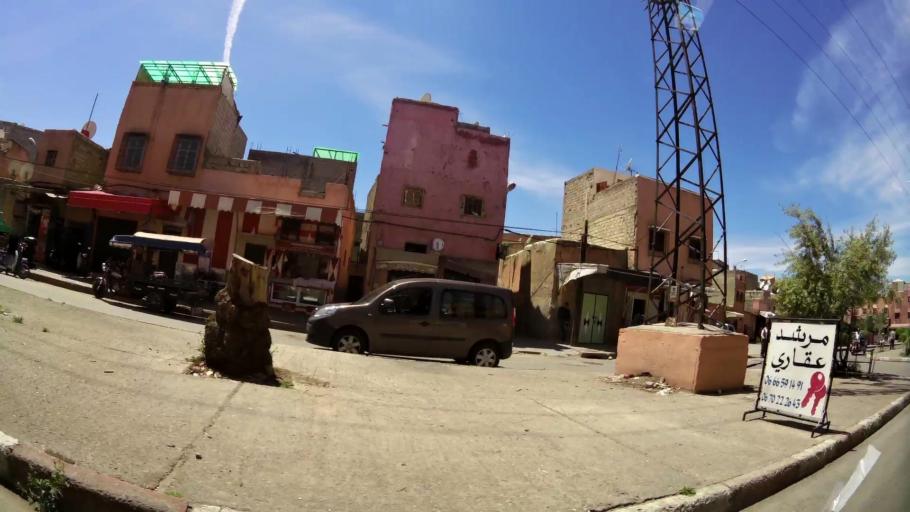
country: MA
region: Marrakech-Tensift-Al Haouz
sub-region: Marrakech
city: Marrakesh
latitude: 31.6359
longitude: -8.0435
